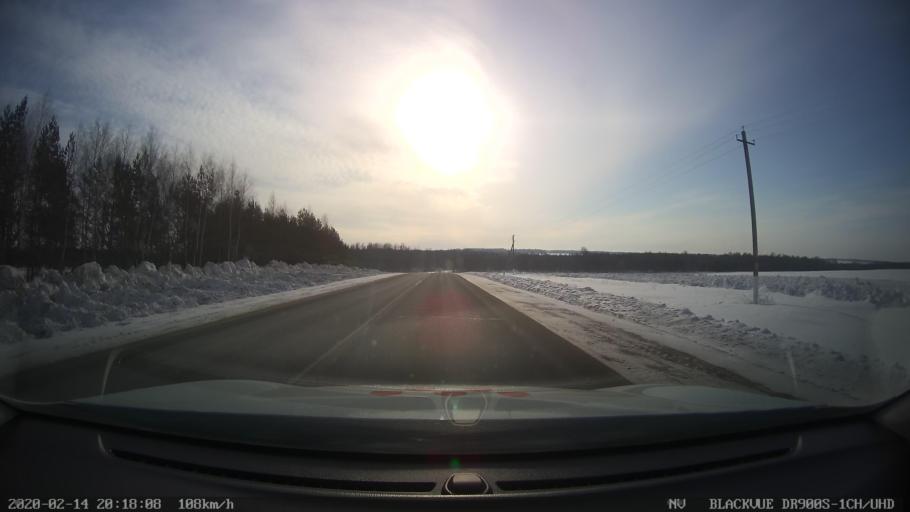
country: RU
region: Tatarstan
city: Verkhniy Uslon
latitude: 55.5904
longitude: 48.8850
